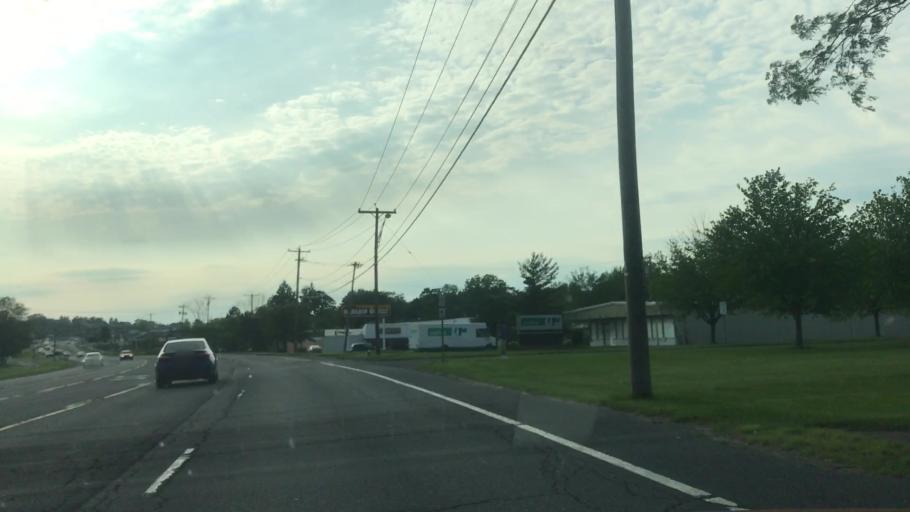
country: US
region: New York
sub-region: Albany County
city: Watervliet
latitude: 42.7374
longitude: -73.7250
